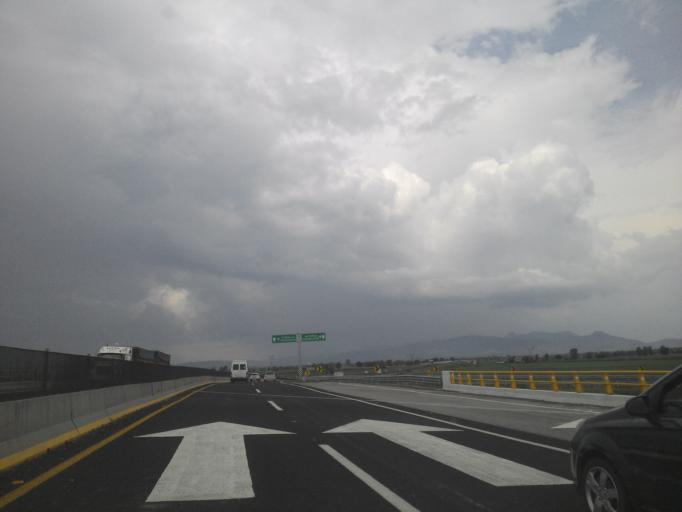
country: MX
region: Hidalgo
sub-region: Tula de Allende
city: Residencial Arboledas
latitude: 20.0991
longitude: -99.2835
